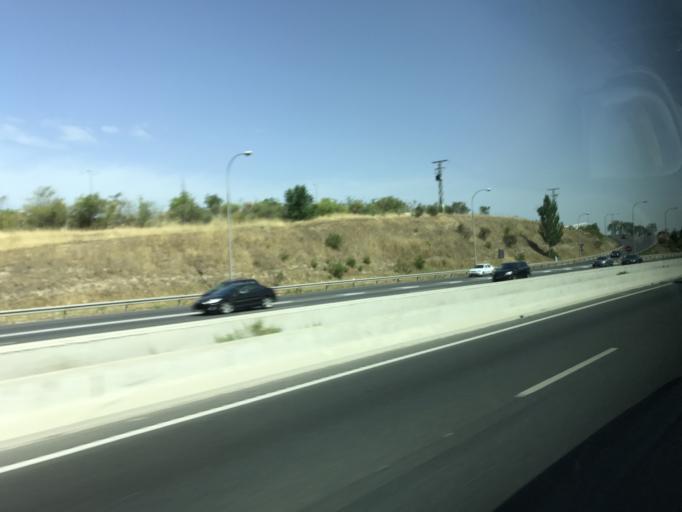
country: ES
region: Madrid
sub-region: Provincia de Madrid
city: San Blas
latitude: 40.4270
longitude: -3.5977
